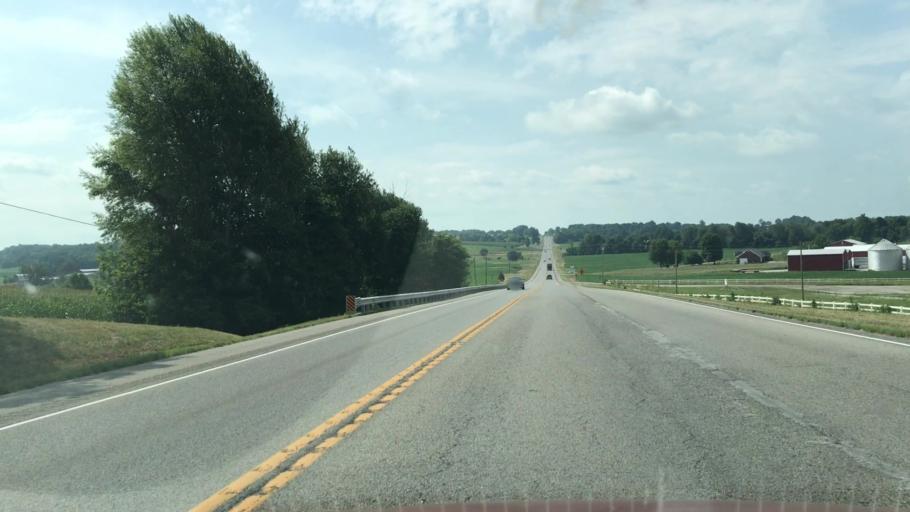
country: US
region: Kentucky
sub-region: Barren County
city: Cave City
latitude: 37.0827
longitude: -85.9689
